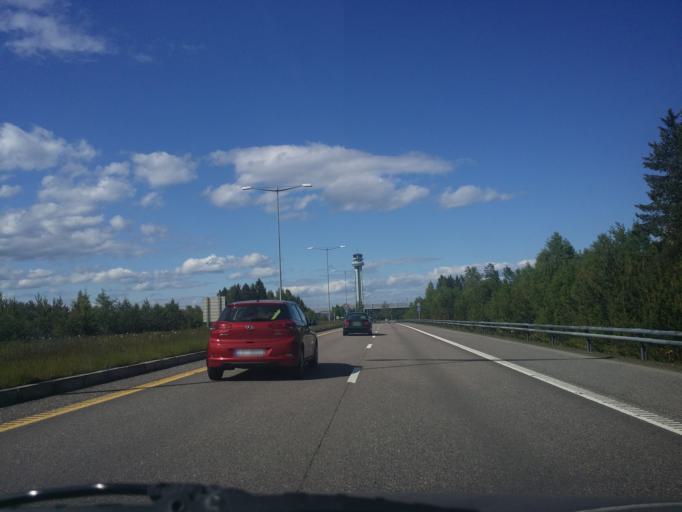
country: NO
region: Akershus
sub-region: Nannestad
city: Teigebyen
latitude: 60.1858
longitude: 11.0942
